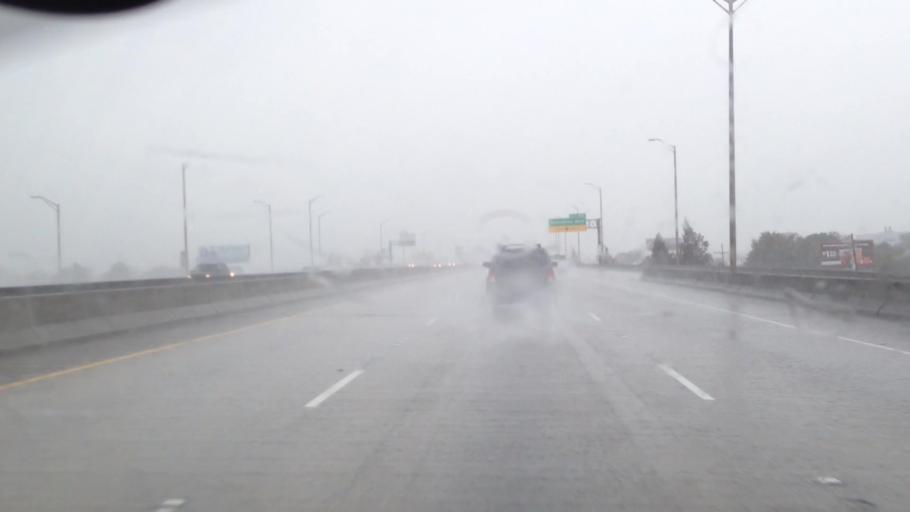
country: US
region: Louisiana
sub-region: Jefferson Parish
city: Gretna
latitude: 29.9087
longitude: -90.0582
